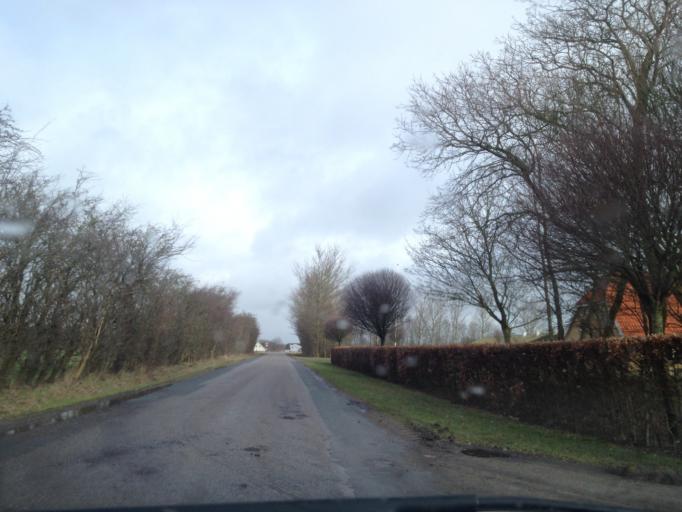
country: DK
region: South Denmark
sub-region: Tonder Kommune
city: Toftlund
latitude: 55.1903
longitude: 9.0493
